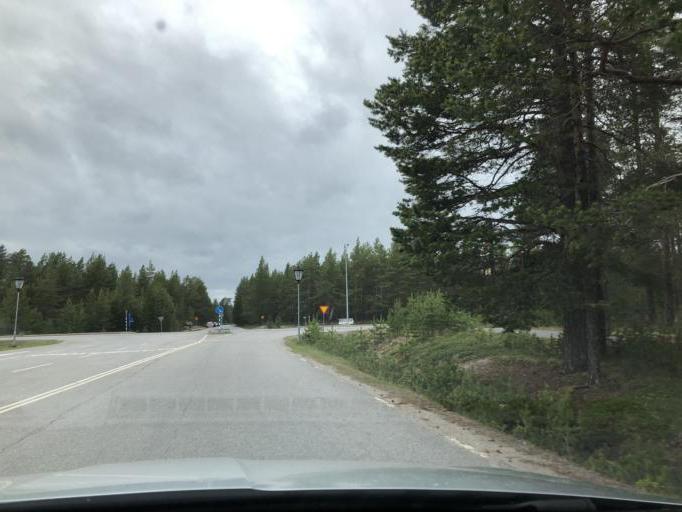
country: SE
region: Norrbotten
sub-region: Pitea Kommun
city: Pitea
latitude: 65.2367
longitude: 21.5276
